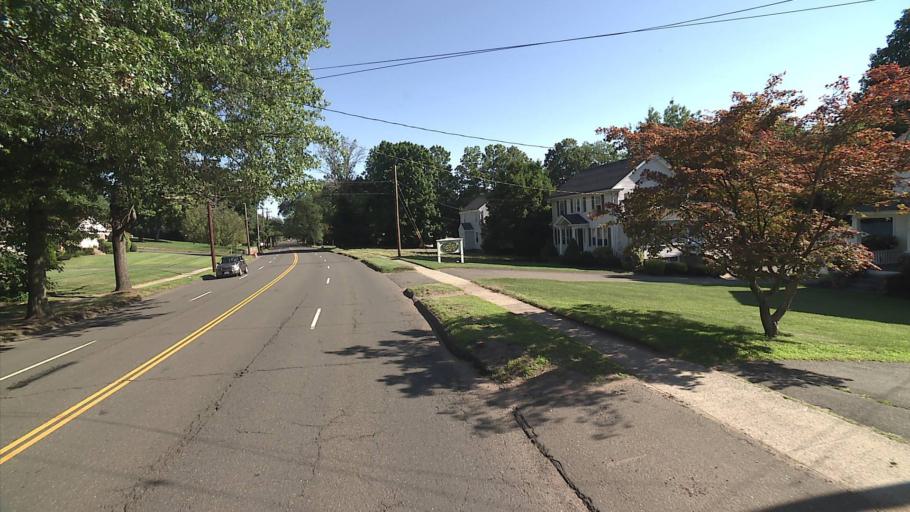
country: US
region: Connecticut
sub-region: New Haven County
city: Hamden
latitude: 41.3950
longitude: -72.8967
